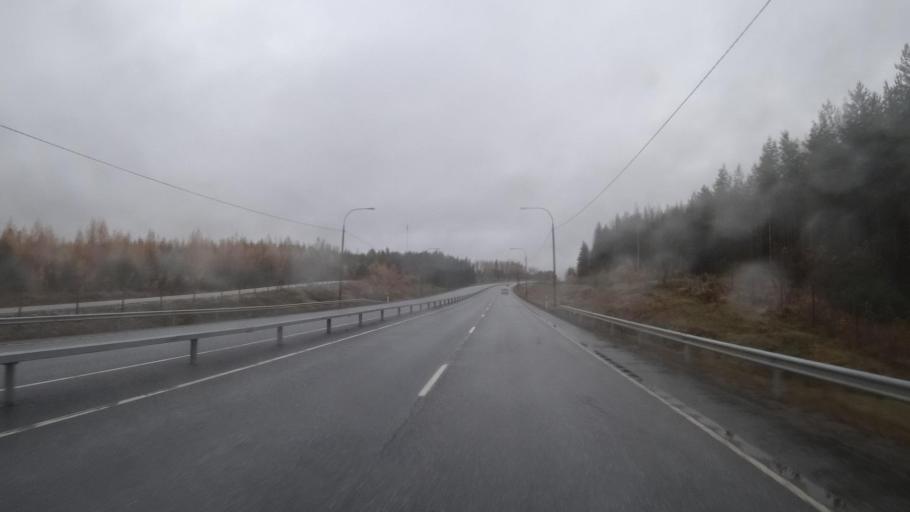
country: FI
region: Northern Savo
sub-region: Varkaus
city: Kangaslampi
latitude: 62.4096
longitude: 28.1706
